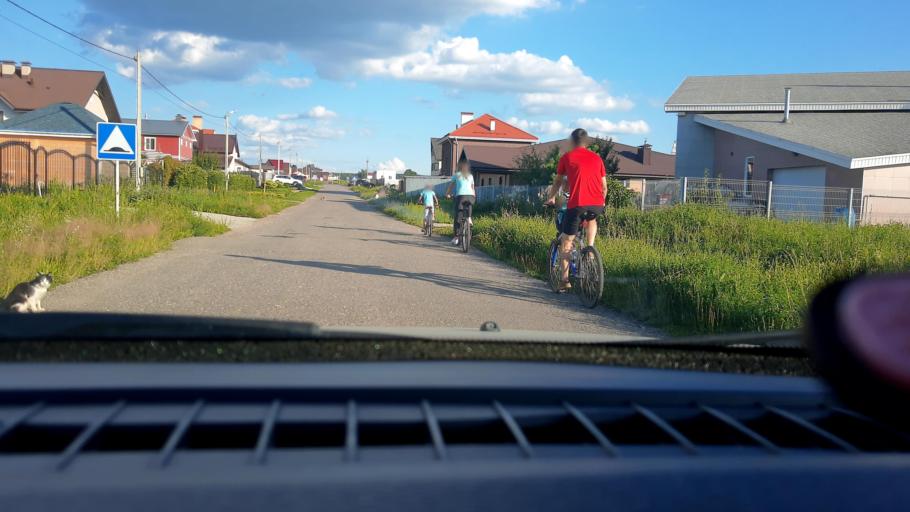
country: RU
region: Nizjnij Novgorod
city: Burevestnik
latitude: 56.0392
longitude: 43.8851
